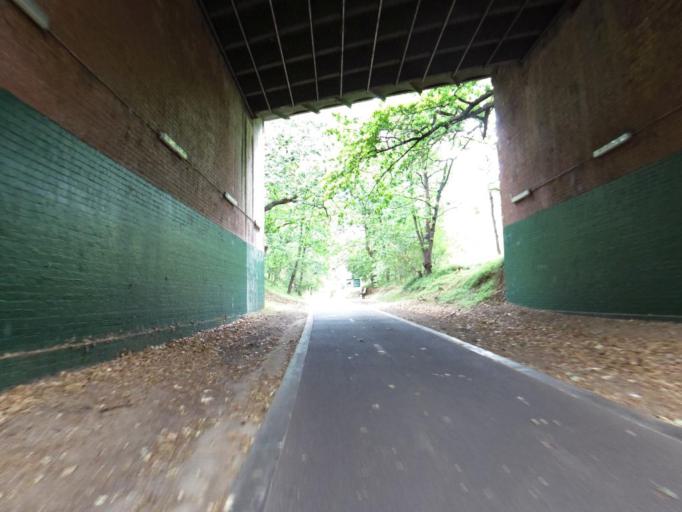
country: AU
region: Victoria
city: Balwyn
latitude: -37.8164
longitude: 145.0654
